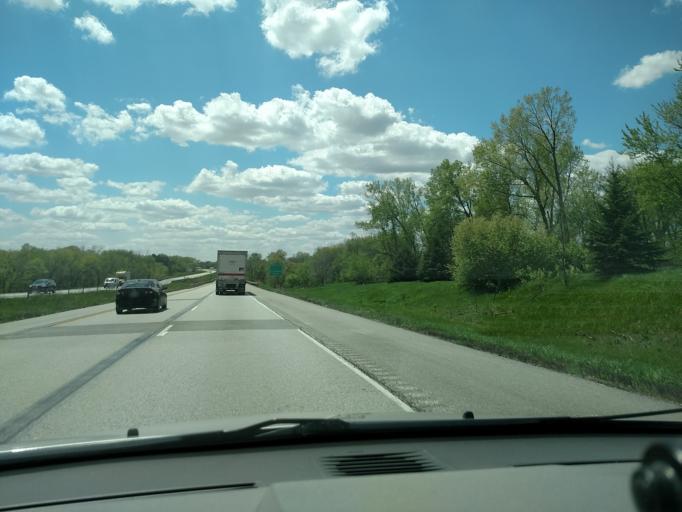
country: US
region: Iowa
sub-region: Polk County
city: Ankeny
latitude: 41.7495
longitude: -93.5744
